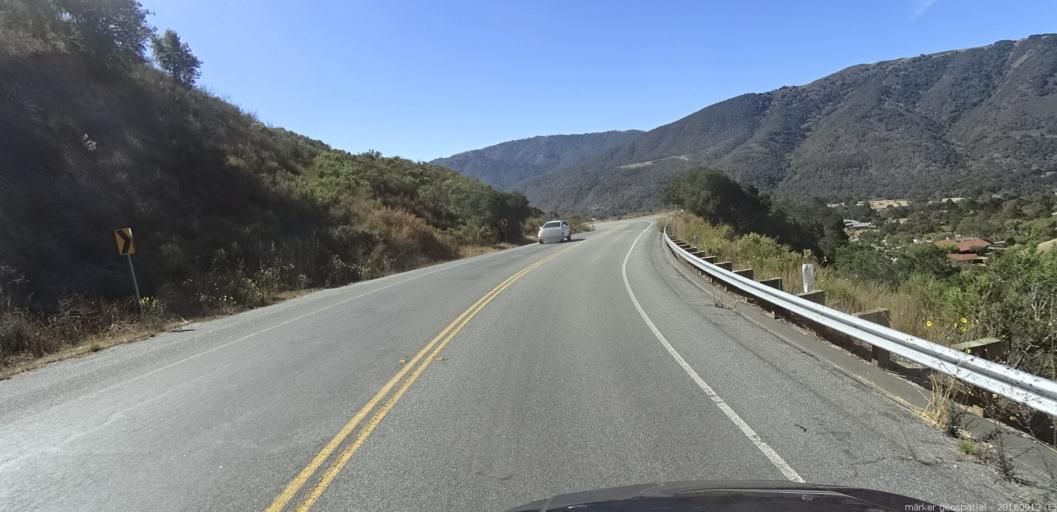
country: US
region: California
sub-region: Monterey County
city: Carmel Valley Village
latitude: 36.5147
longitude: -121.7562
